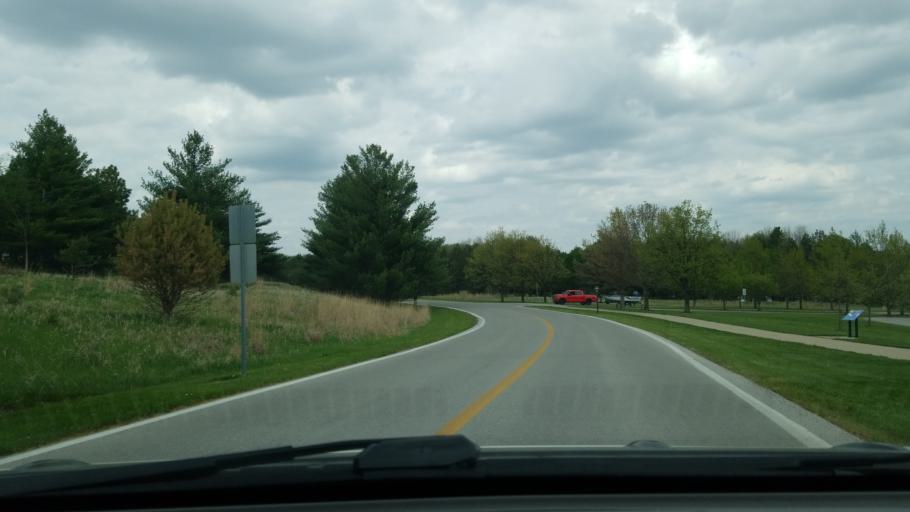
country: US
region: Nebraska
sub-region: Sarpy County
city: Chalco
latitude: 41.1651
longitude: -96.1575
